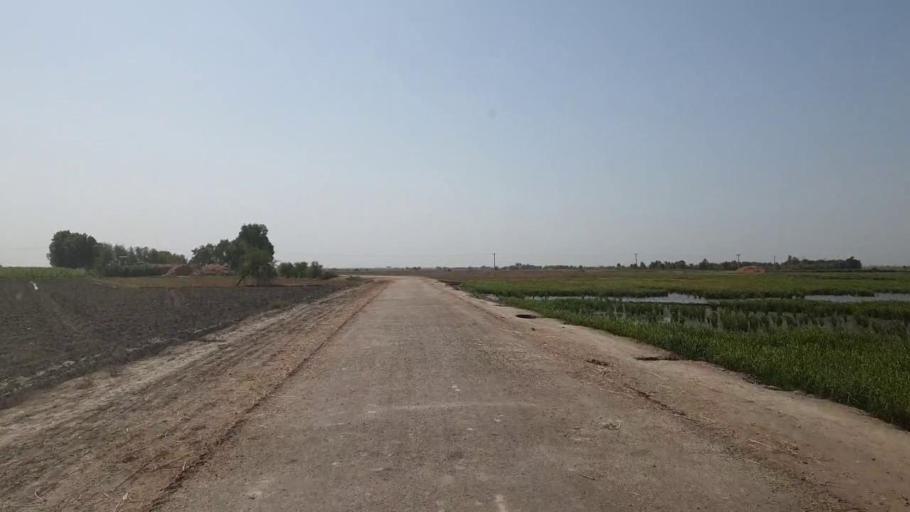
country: PK
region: Sindh
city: Tando Bago
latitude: 24.7666
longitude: 69.0226
